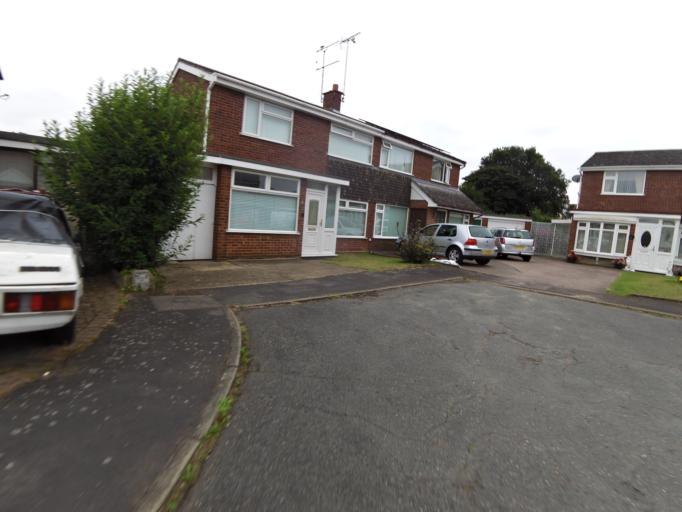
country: GB
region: England
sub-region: Suffolk
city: Bramford
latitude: 52.0757
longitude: 1.0992
